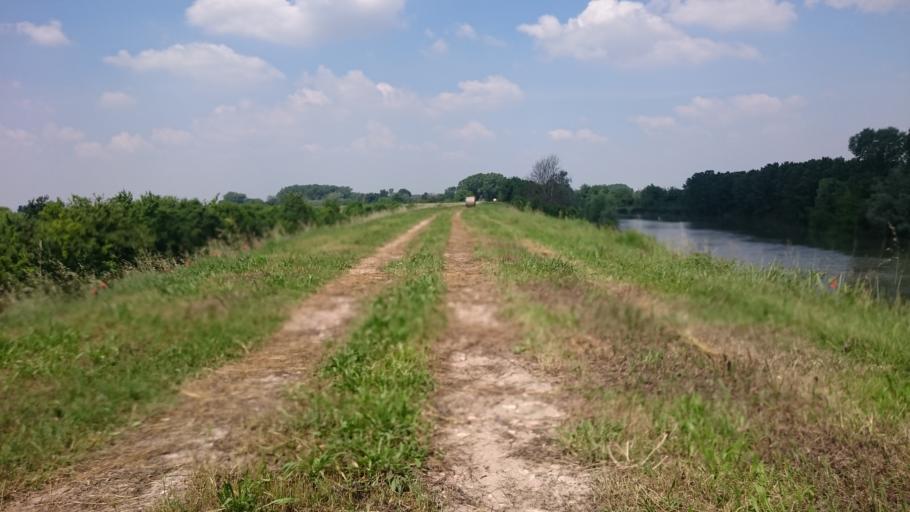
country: IT
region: Lombardy
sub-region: Provincia di Mantova
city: Bagnolo San Vito
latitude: 45.1069
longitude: 10.8802
